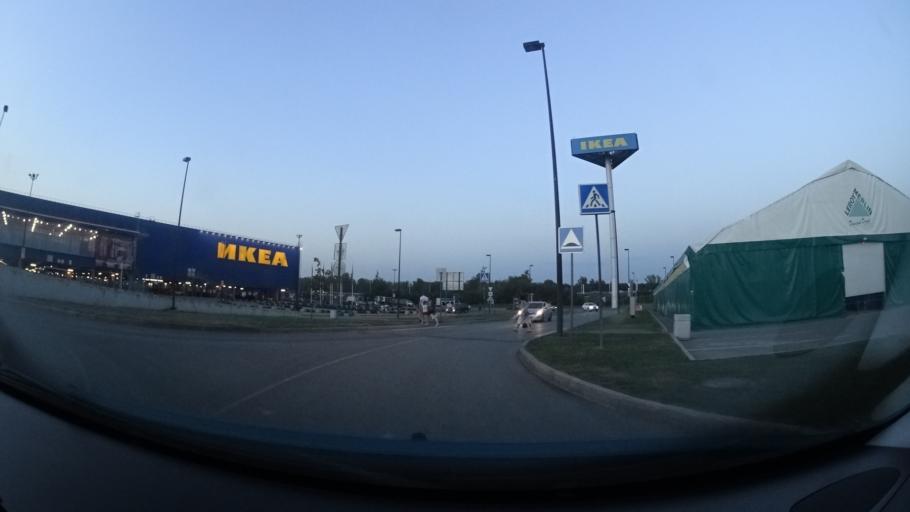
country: RU
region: Bashkortostan
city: Ufa
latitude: 54.6717
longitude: 55.9296
